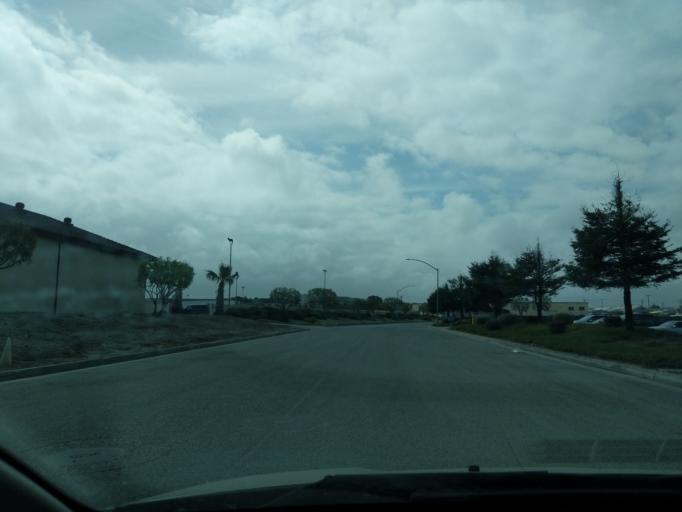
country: US
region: California
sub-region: Monterey County
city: Castroville
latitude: 36.7622
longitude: -121.7431
